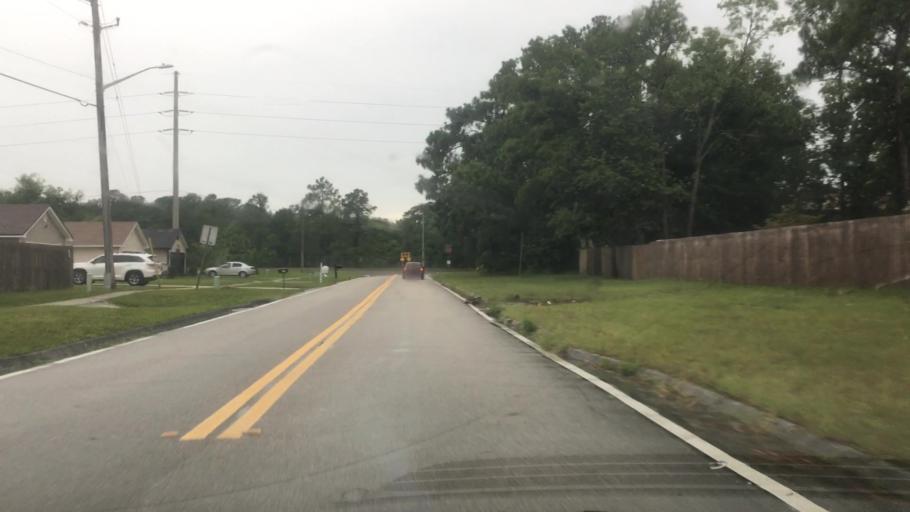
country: US
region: Florida
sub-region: Duval County
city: Jacksonville
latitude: 30.3381
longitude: -81.5367
